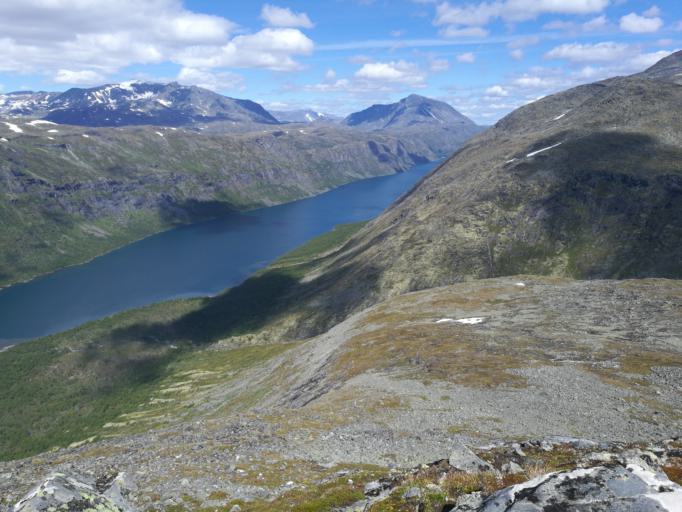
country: NO
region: Oppland
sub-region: Vang
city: Vang
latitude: 61.4356
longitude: 8.4949
